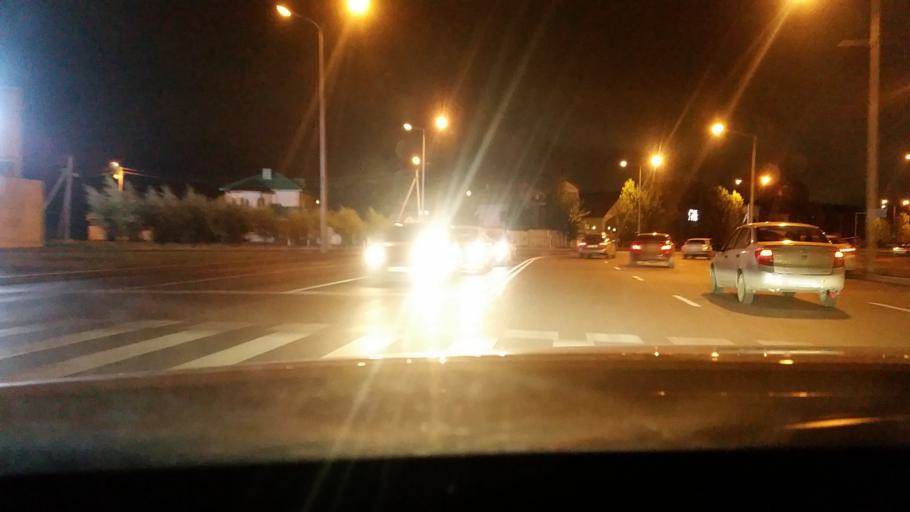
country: KZ
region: Astana Qalasy
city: Astana
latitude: 51.1477
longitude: 71.5038
